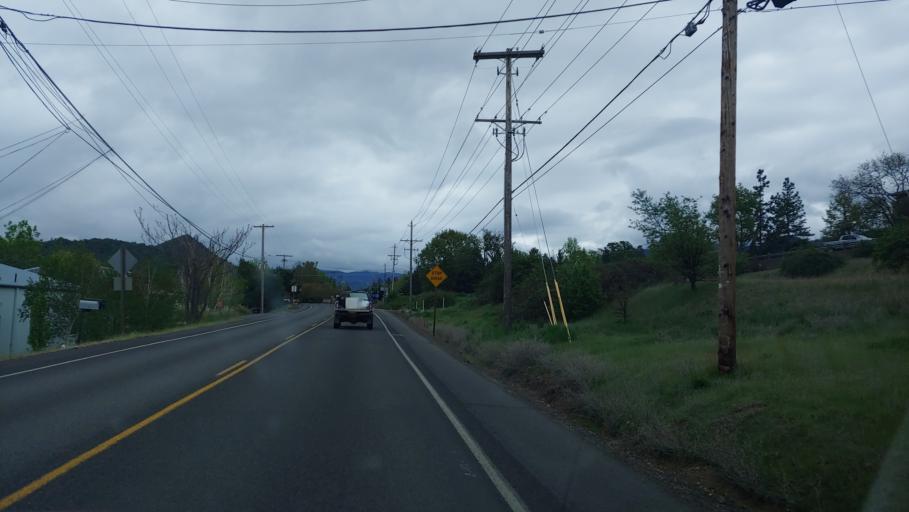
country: US
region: Oregon
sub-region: Jackson County
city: Ashland
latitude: 42.1868
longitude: -122.6601
